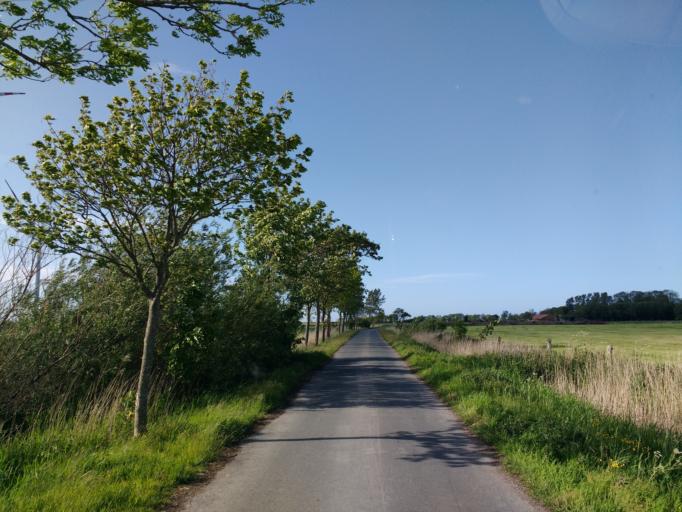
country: DE
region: Lower Saxony
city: Schillig
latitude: 53.6953
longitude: 7.9393
